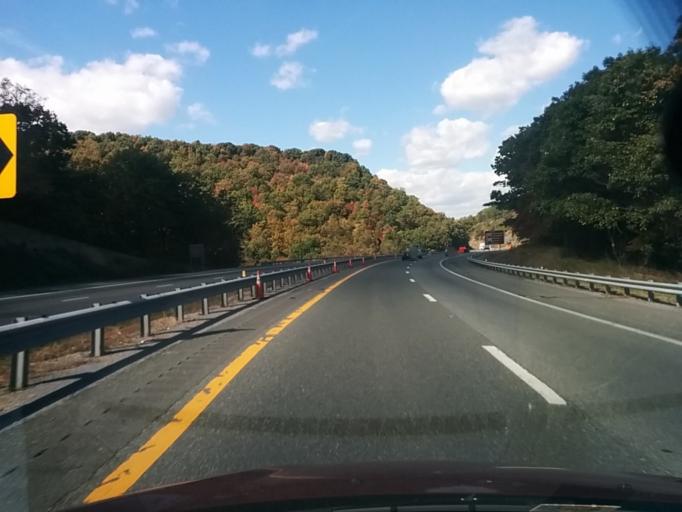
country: US
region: Virginia
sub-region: City of Waynesboro
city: Waynesboro
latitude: 38.0346
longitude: -78.8693
